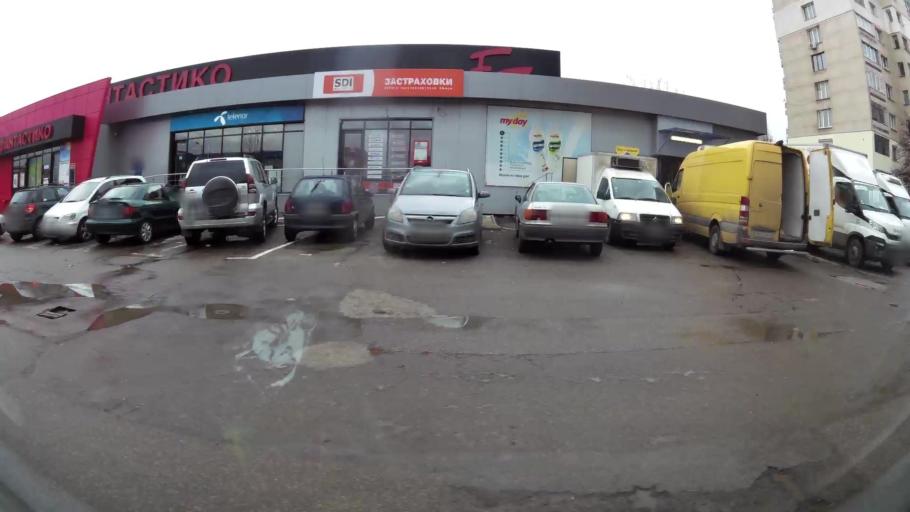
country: BG
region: Sofiya
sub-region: Obshtina Bozhurishte
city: Bozhurishte
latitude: 42.7300
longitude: 23.2532
